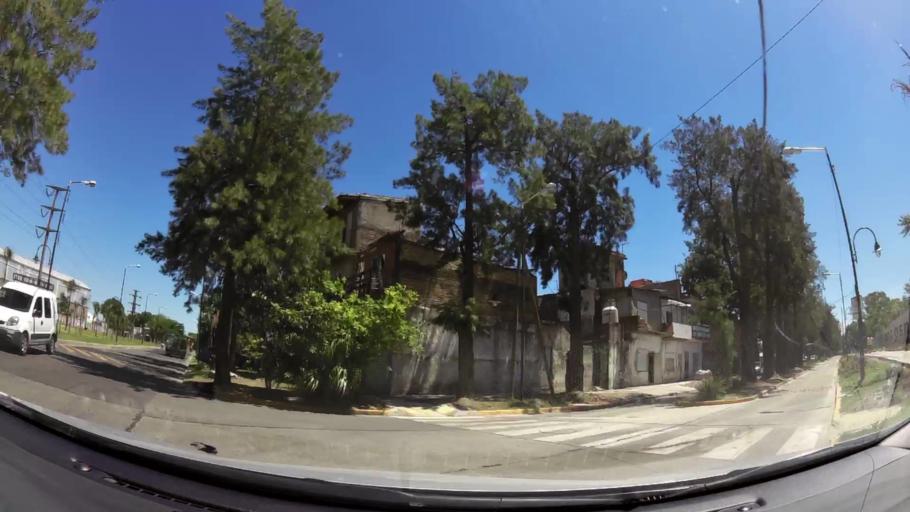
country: AR
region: Buenos Aires
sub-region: Partido de Tigre
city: Tigre
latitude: -34.4581
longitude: -58.5559
